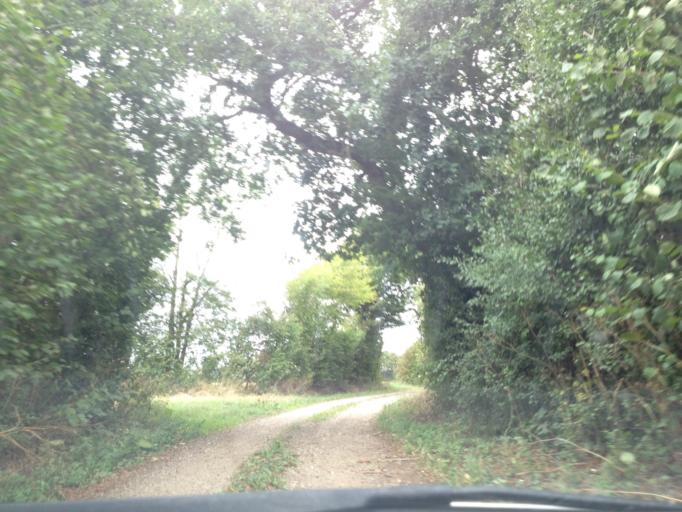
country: DK
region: South Denmark
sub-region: Haderslev Kommune
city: Starup
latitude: 55.2993
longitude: 9.5538
